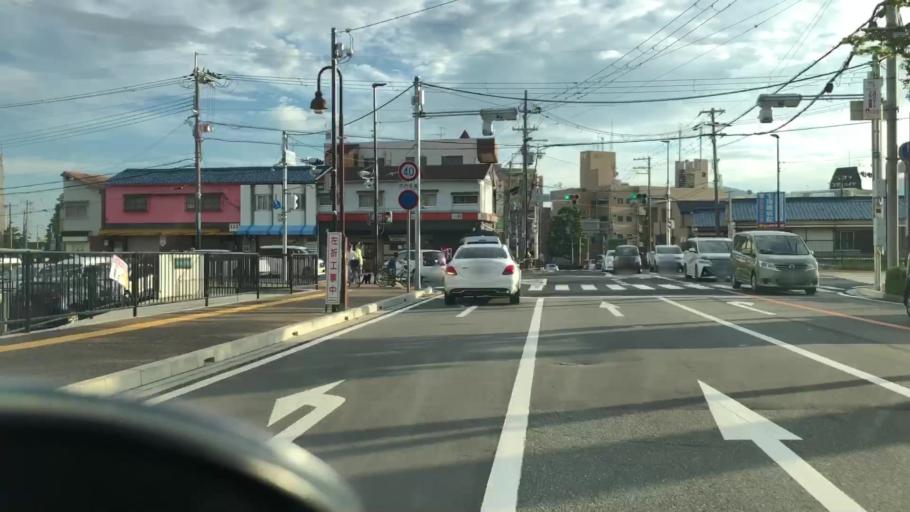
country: JP
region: Hyogo
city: Takarazuka
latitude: 34.7994
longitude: 135.3593
